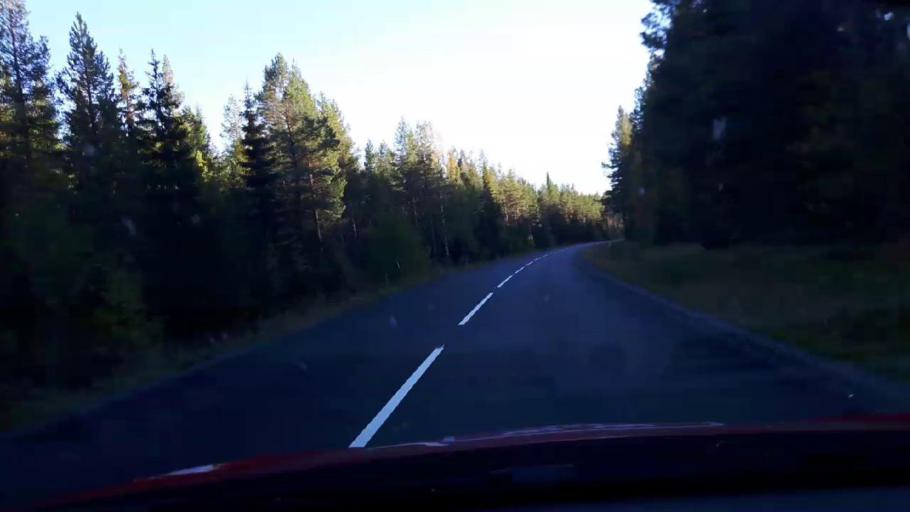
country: SE
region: Jaemtland
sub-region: OEstersunds Kommun
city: Lit
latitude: 63.4708
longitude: 14.8773
